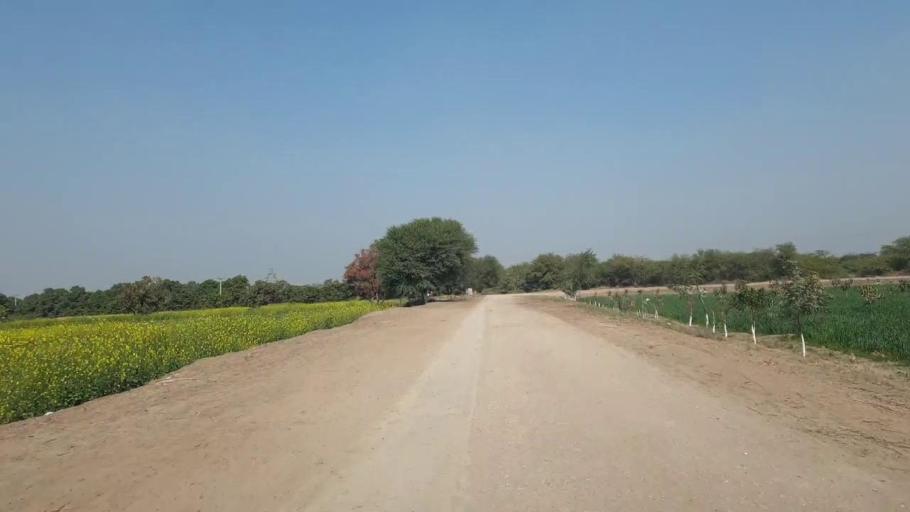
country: PK
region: Sindh
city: Mirwah Gorchani
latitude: 25.3830
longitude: 68.9318
